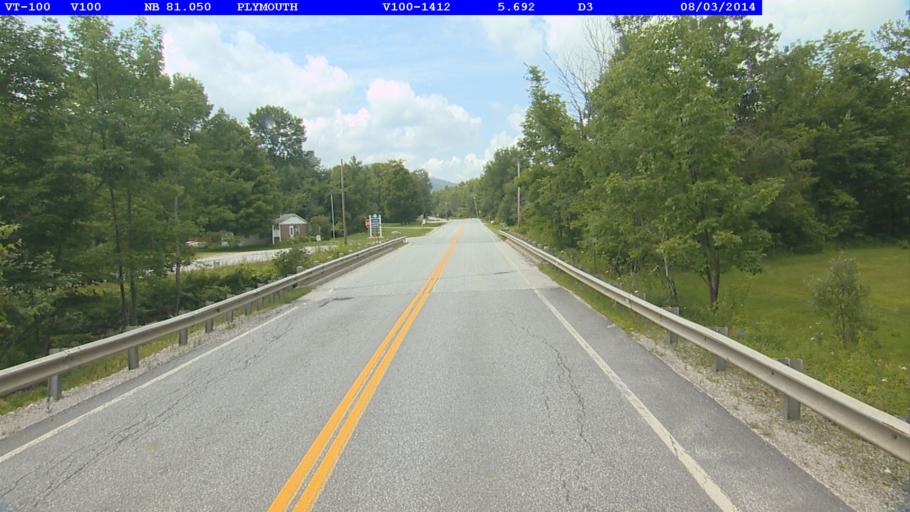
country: US
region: Vermont
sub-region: Windsor County
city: Woodstock
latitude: 43.5347
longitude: -72.7422
